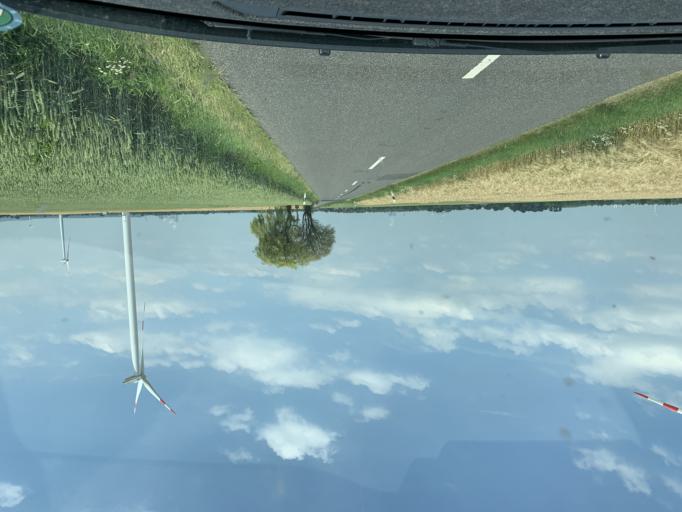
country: DE
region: North Rhine-Westphalia
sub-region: Regierungsbezirk Koln
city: Titz
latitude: 50.9770
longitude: 6.4868
